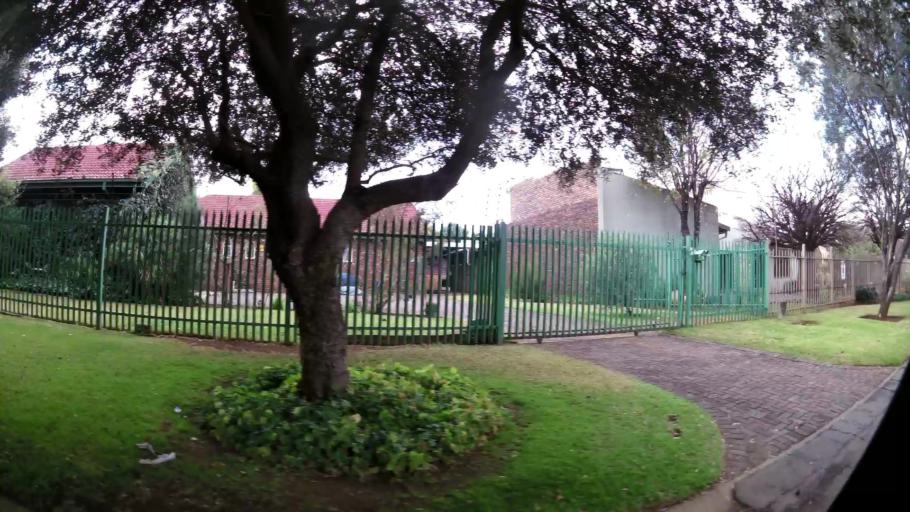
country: ZA
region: Gauteng
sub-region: Sedibeng District Municipality
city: Vanderbijlpark
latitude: -26.7358
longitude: 27.8517
